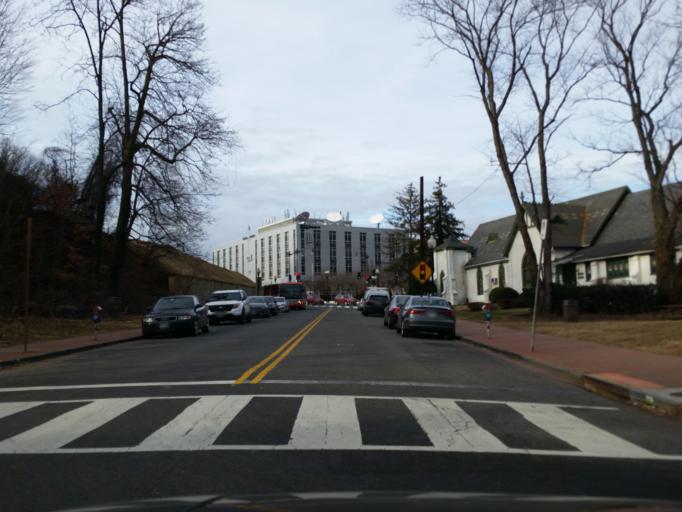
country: US
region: Washington, D.C.
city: Washington, D.C.
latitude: 38.9167
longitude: -77.0693
